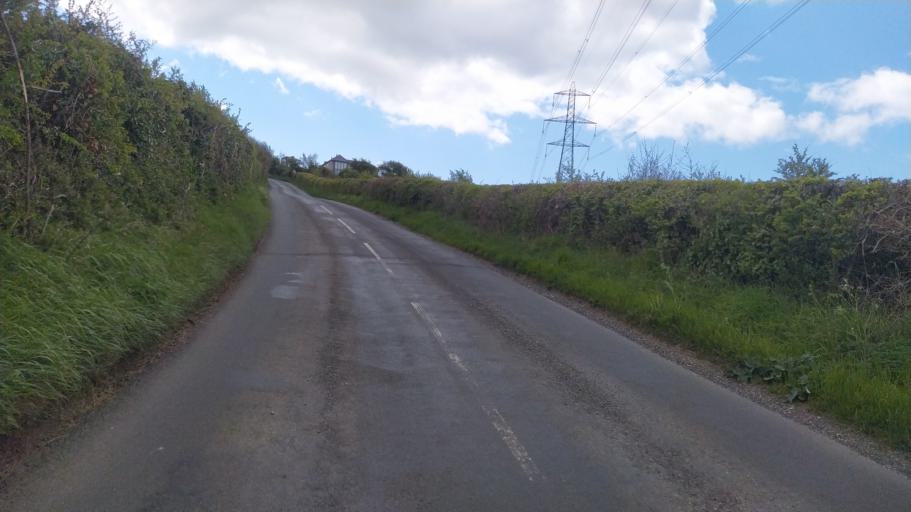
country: GB
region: England
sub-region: Dorset
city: Chickerell
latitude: 50.6356
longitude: -2.4872
